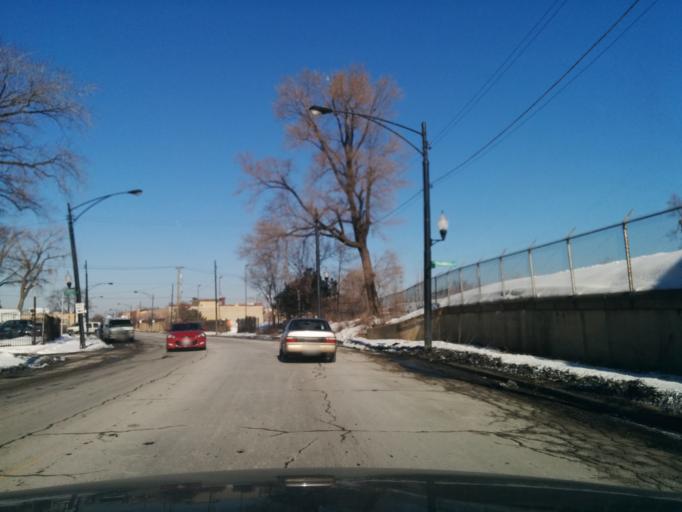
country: US
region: Illinois
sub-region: Cook County
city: Cicero
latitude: 41.9006
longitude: -87.7123
